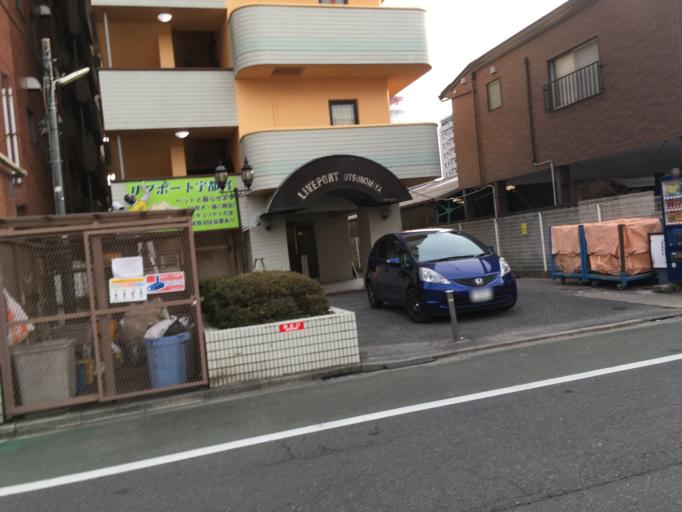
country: JP
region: Tochigi
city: Utsunomiya-shi
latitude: 36.5589
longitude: 139.8907
